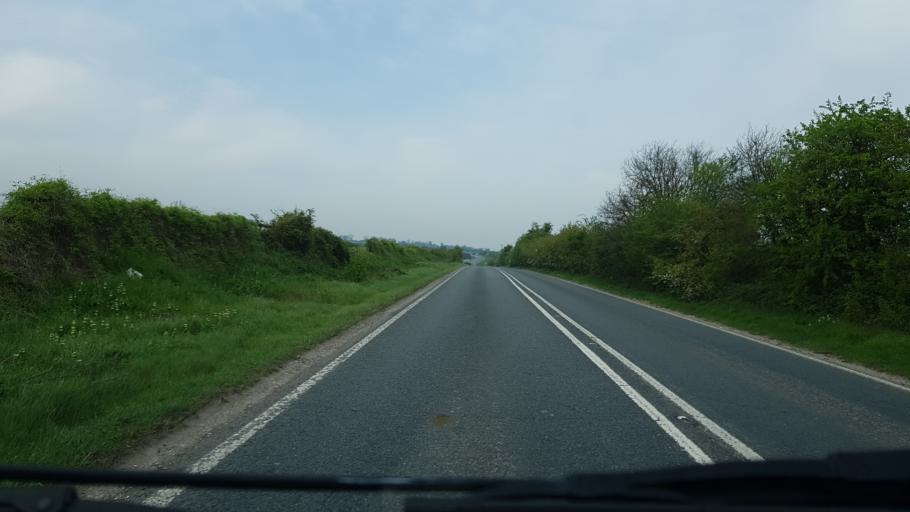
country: GB
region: England
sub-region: Hampshire
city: Basingstoke
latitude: 51.2847
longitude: -1.1353
